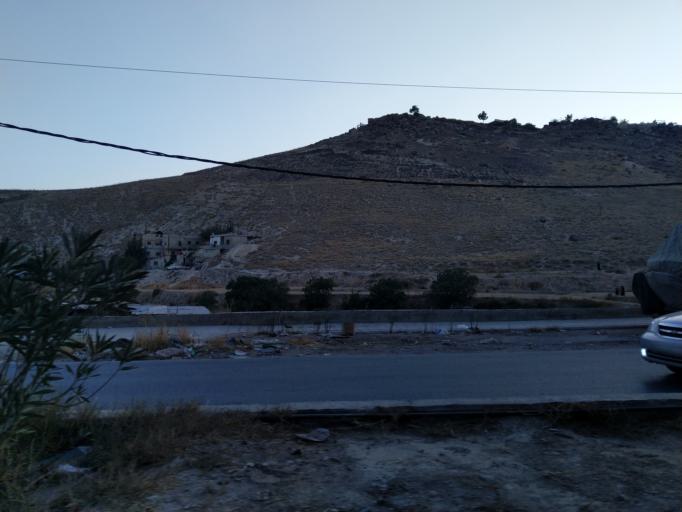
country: SY
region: Rif-dimashq
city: At Tall
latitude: 33.5738
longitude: 36.3046
